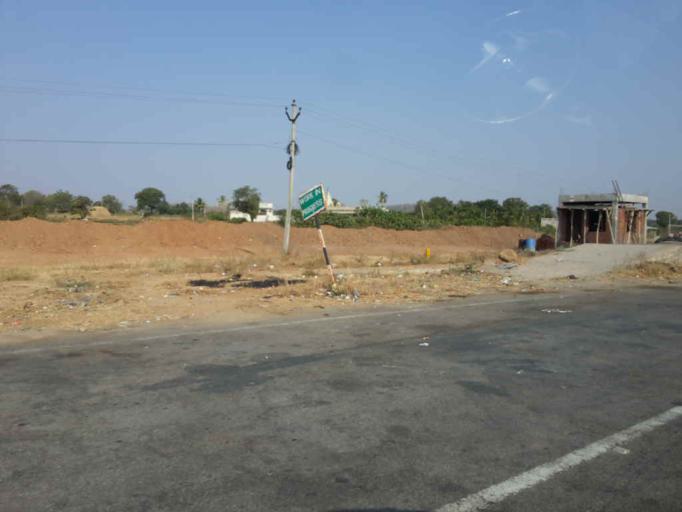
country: IN
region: Telangana
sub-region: Nizamabad District
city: Nizamabad
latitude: 18.5391
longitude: 78.2399
